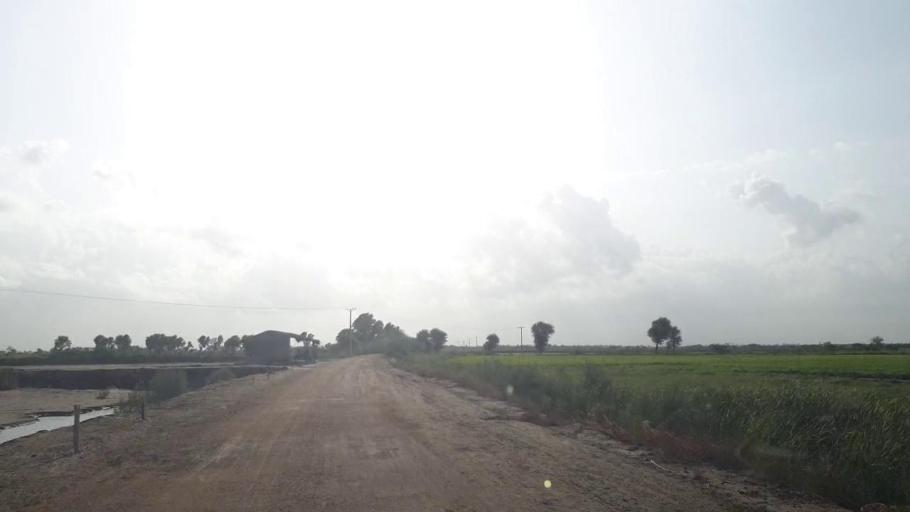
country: PK
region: Sindh
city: Kadhan
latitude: 24.6266
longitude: 69.0920
